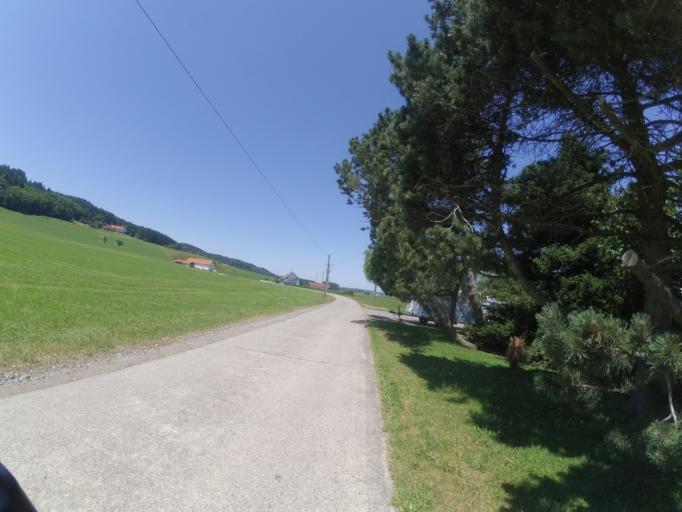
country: DE
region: Bavaria
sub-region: Swabia
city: Bohen
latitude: 47.8663
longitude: 10.3435
